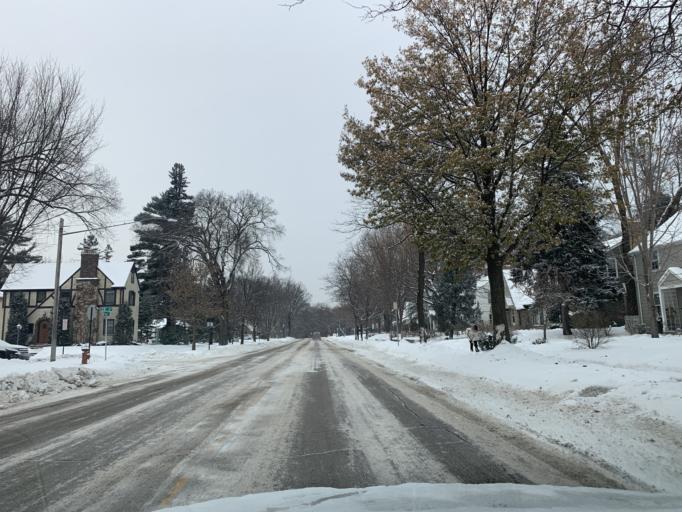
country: US
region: Minnesota
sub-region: Hennepin County
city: Saint Louis Park
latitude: 44.9517
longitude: -93.3288
